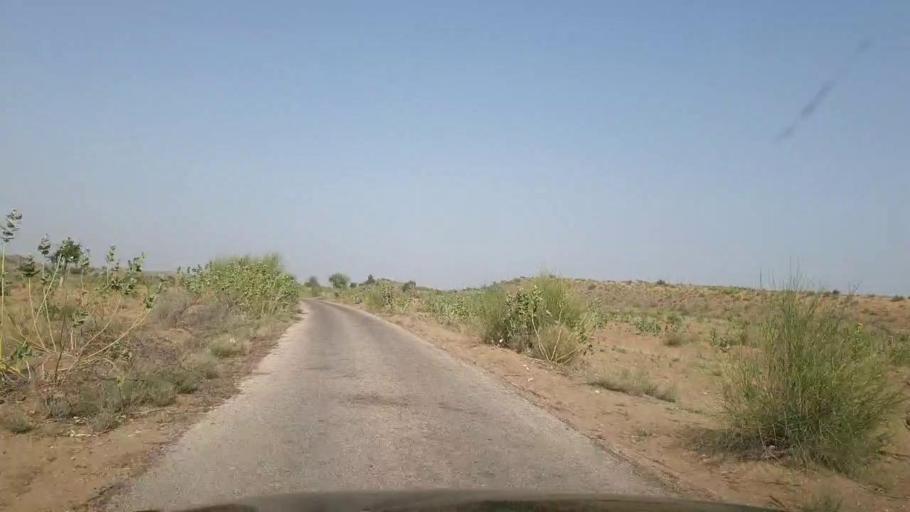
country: PK
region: Sindh
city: Islamkot
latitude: 25.1208
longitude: 70.4426
